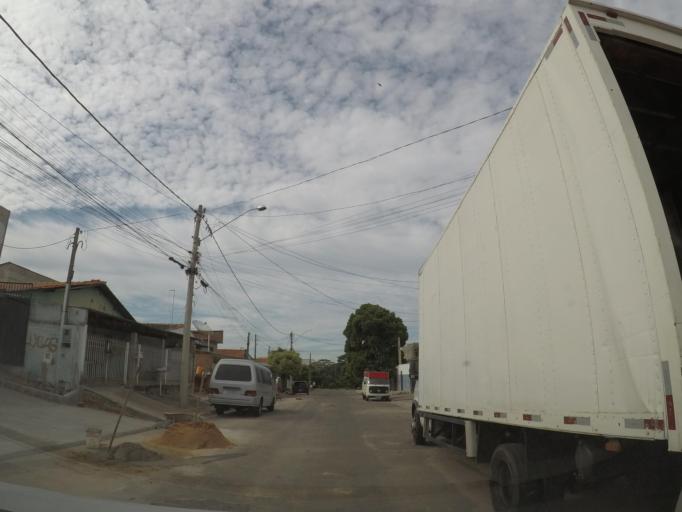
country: BR
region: Sao Paulo
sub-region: Hortolandia
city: Hortolandia
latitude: -22.8200
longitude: -47.1948
